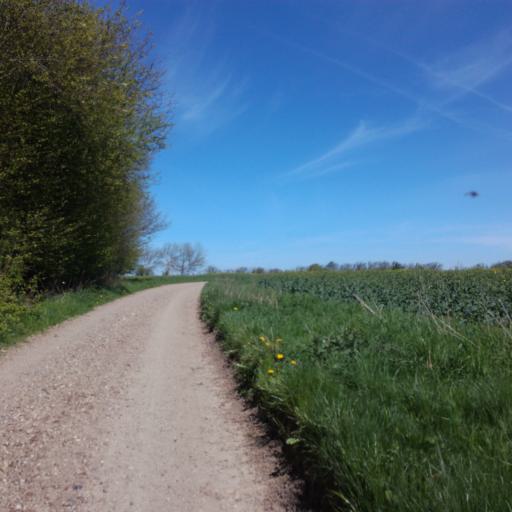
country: DK
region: South Denmark
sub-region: Vejle Kommune
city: Borkop
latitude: 55.6126
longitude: 9.6852
